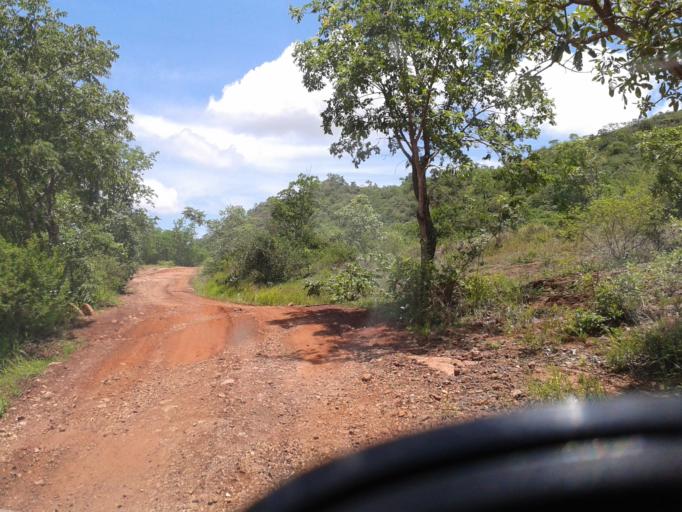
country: BR
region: Minas Gerais
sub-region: Santa Vitoria
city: Santa Vitoria
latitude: -18.9843
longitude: -49.8962
